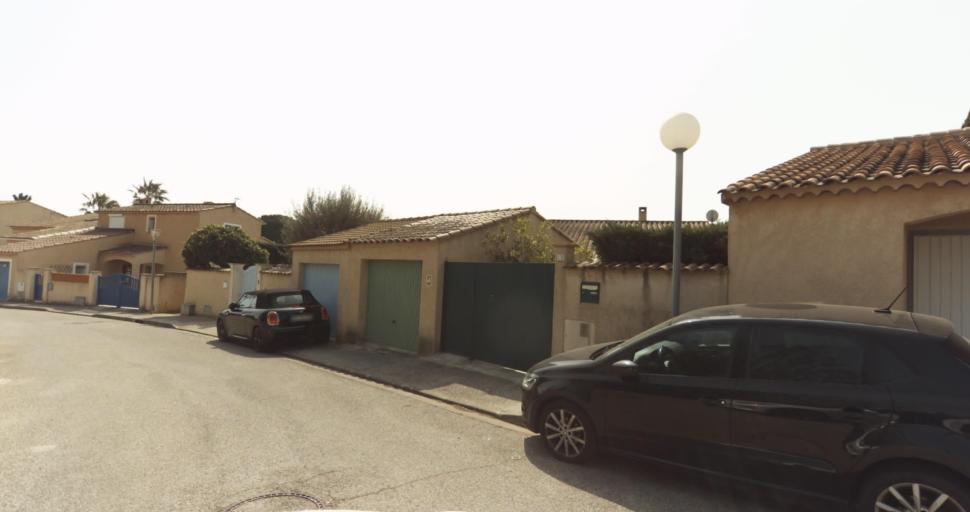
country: FR
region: Provence-Alpes-Cote d'Azur
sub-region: Departement du Var
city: Bormes-les-Mimosas
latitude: 43.1402
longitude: 6.3452
